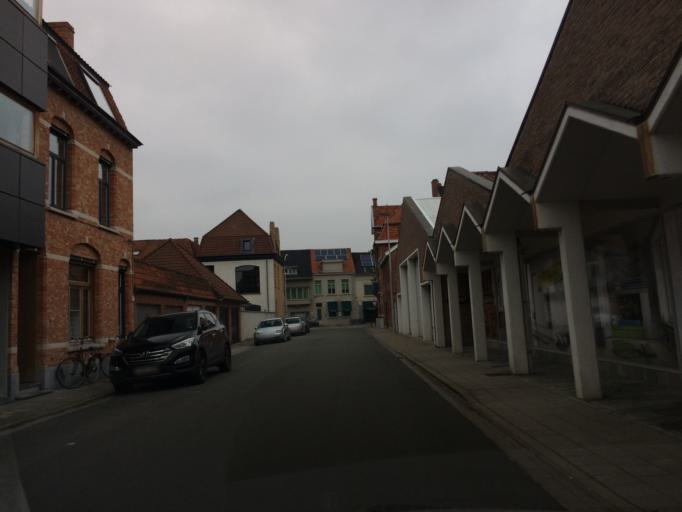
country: BE
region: Flanders
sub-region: Provincie West-Vlaanderen
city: Sint-Kruis
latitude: 51.2130
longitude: 3.2482
